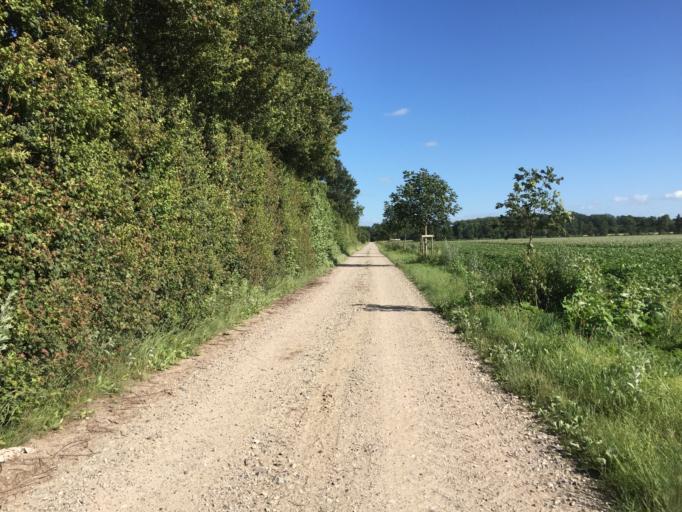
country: DK
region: South Denmark
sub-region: Kerteminde Kommune
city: Langeskov
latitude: 55.3728
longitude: 10.5427
